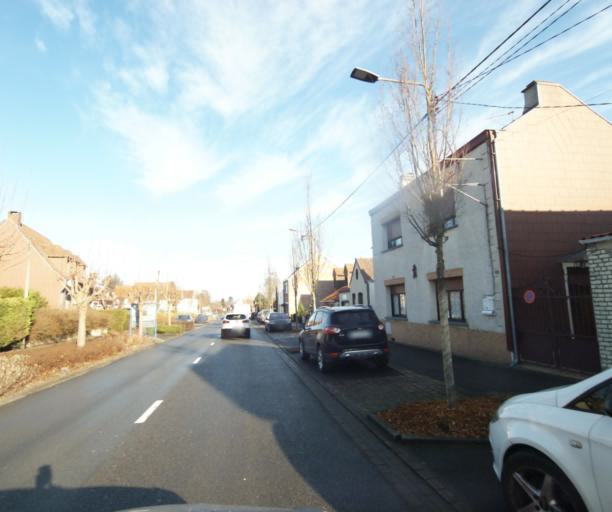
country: FR
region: Nord-Pas-de-Calais
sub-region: Departement du Nord
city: Famars
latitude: 50.3253
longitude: 3.5207
